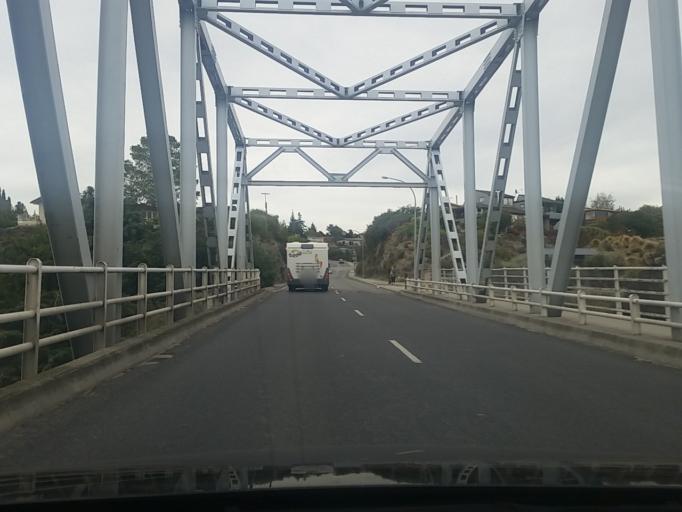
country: NZ
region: Otago
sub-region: Queenstown-Lakes District
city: Wanaka
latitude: -45.2589
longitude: 169.3903
